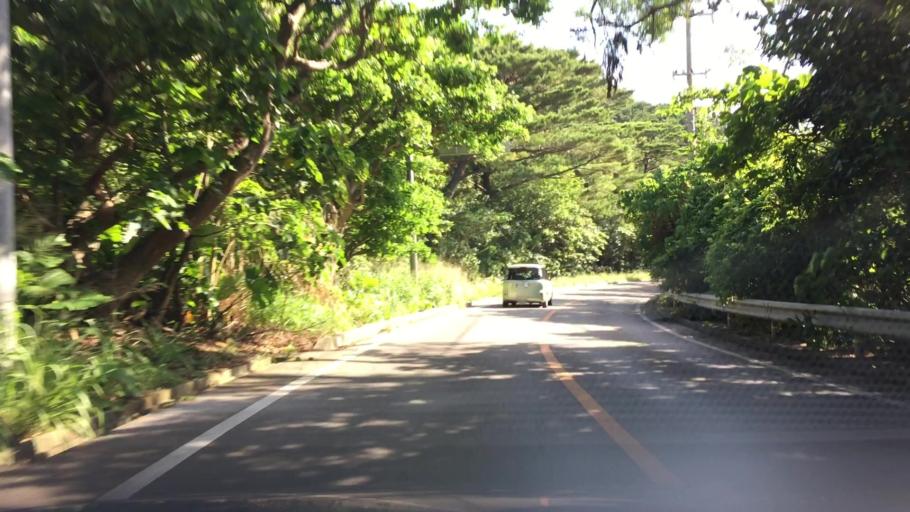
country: JP
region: Okinawa
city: Ishigaki
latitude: 24.4441
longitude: 124.1253
